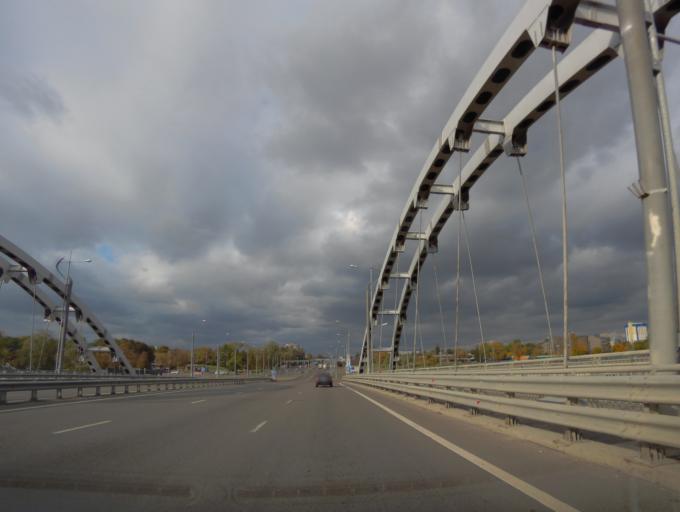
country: BY
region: Brest
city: Brest
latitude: 52.0834
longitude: 23.6709
